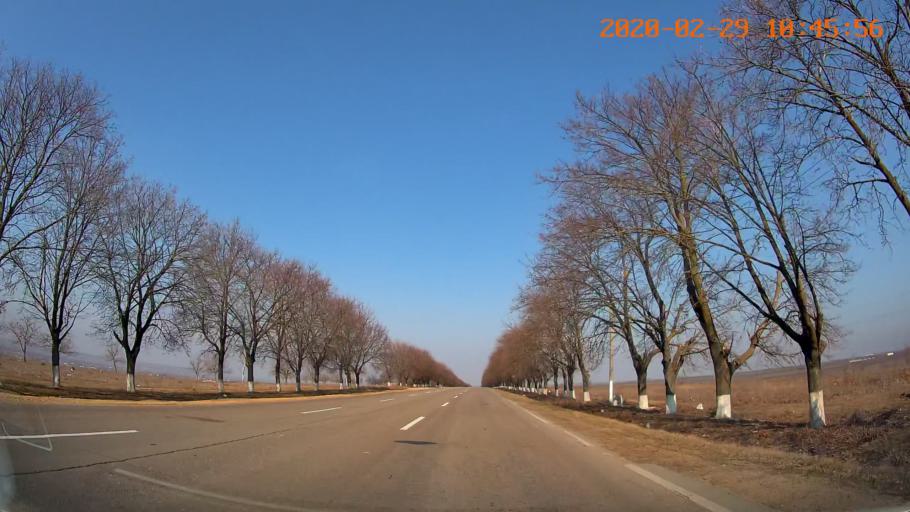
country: MD
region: Telenesti
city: Grigoriopol
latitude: 47.0799
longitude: 29.3780
